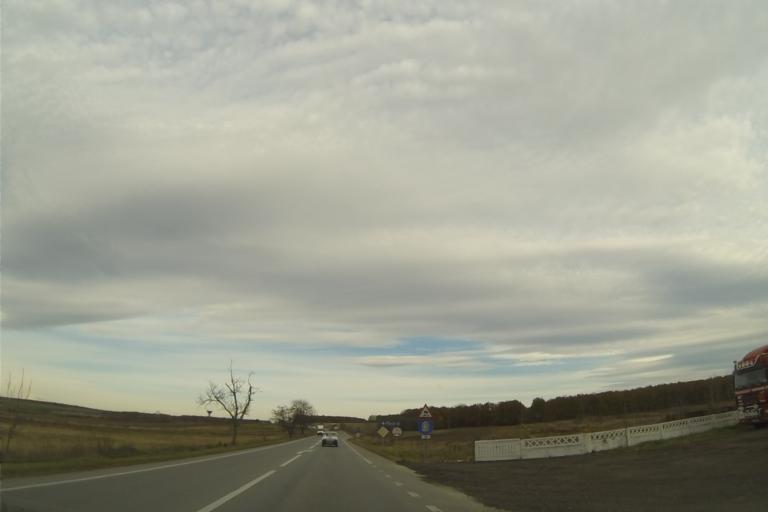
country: RO
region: Olt
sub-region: Comuna Scornicesti
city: Scornicesti
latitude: 44.5528
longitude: 24.5614
